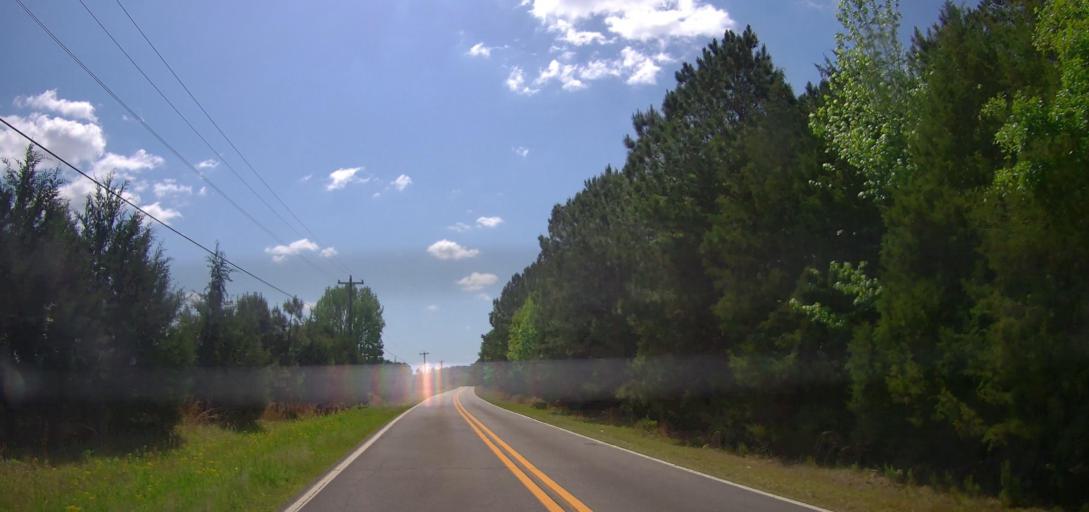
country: US
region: Georgia
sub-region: Putnam County
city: Eatonton
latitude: 33.3253
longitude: -83.2999
